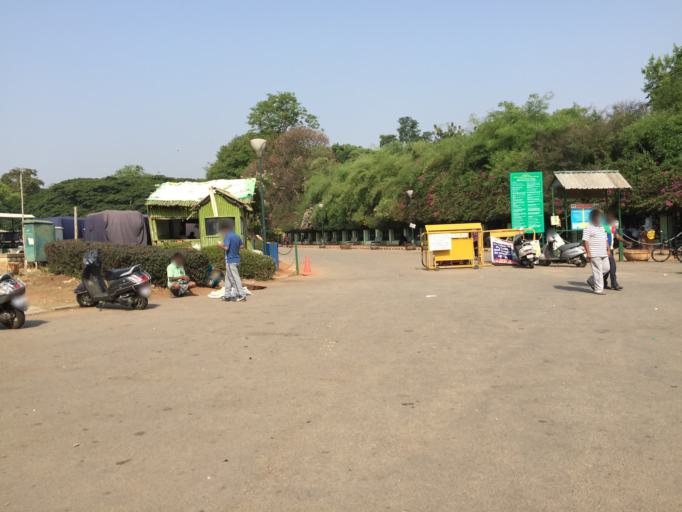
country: IN
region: Karnataka
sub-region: Bangalore Urban
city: Bangalore
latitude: 12.9497
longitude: 77.5898
